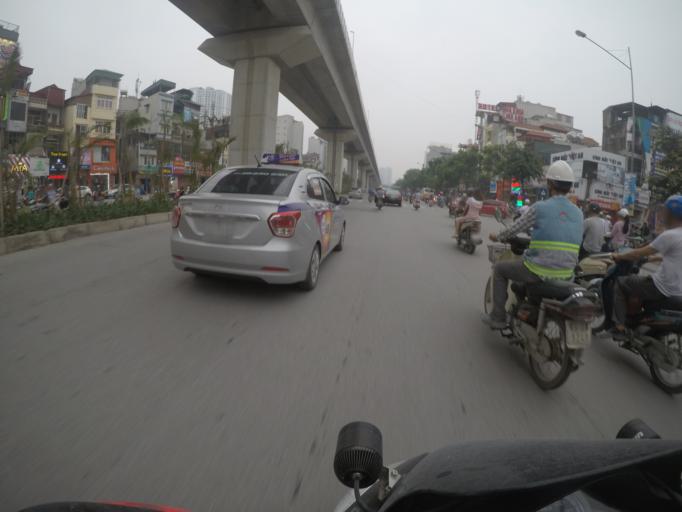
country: VN
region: Ha Noi
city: Thanh Xuan
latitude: 20.9981
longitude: 105.8131
